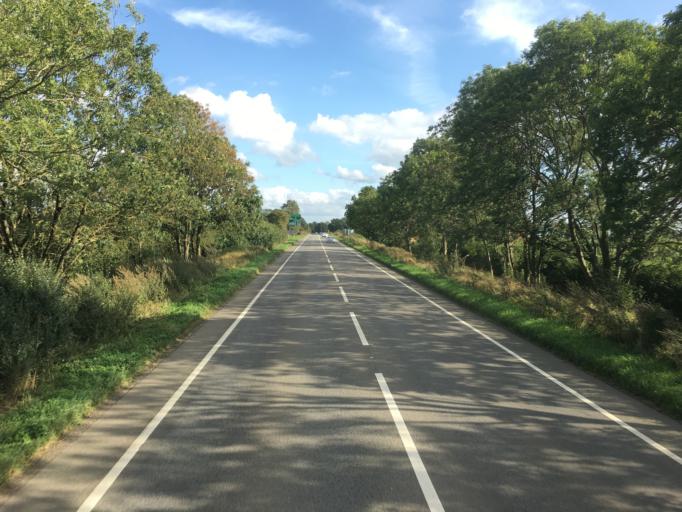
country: GB
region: England
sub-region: Leicestershire
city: Lutterworth
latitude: 52.4269
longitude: -1.2292
